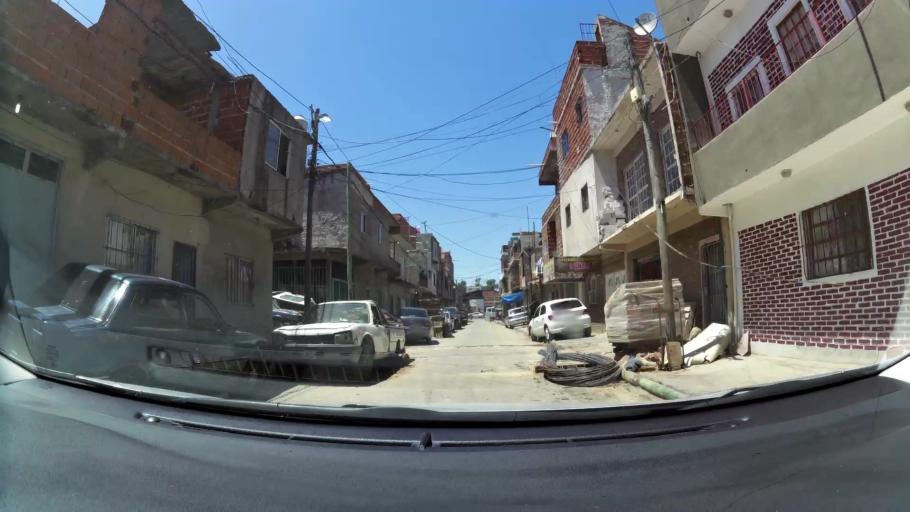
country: AR
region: Buenos Aires
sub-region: Partido de Avellaneda
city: Avellaneda
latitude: -34.6569
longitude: -58.4006
